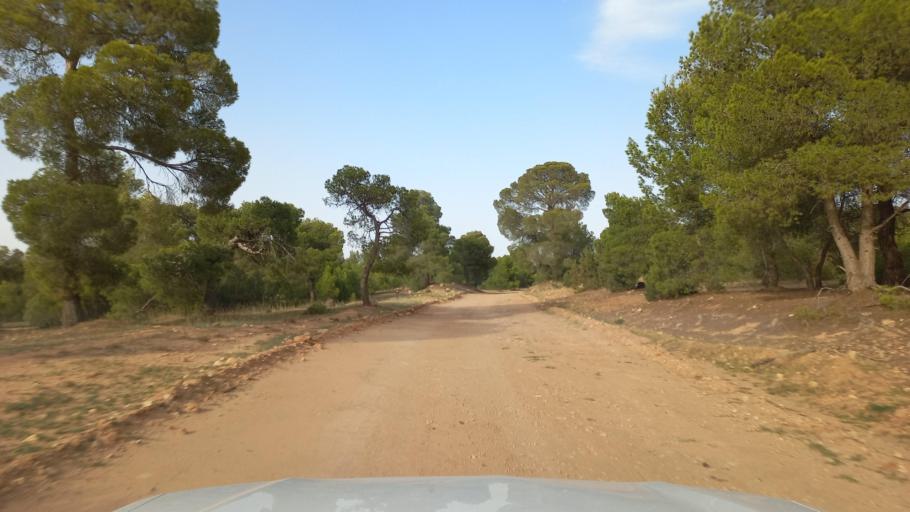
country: TN
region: Al Qasrayn
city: Kasserine
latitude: 35.3410
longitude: 8.8589
